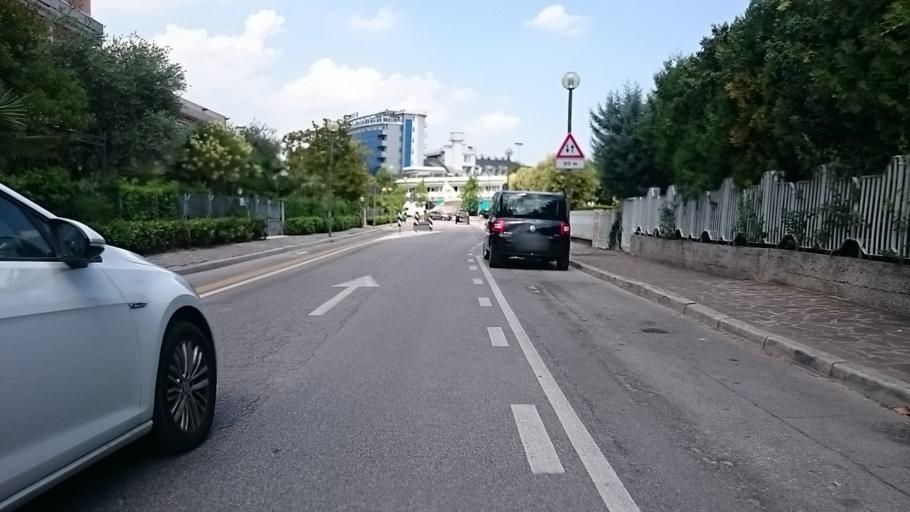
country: IT
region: Veneto
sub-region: Provincia di Padova
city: Abano Terme
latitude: 45.3474
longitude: 11.7858
